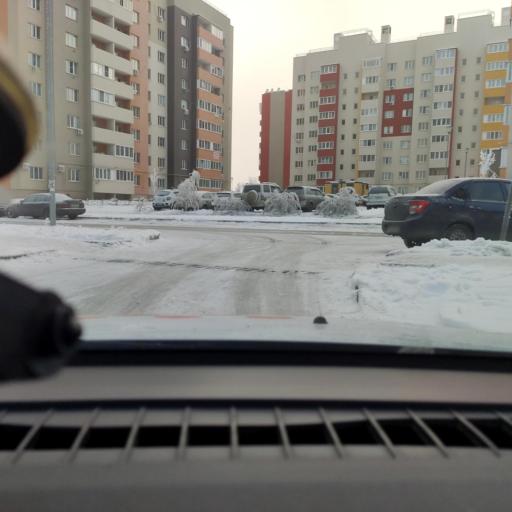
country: RU
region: Samara
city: Samara
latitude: 53.0931
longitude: 50.1601
